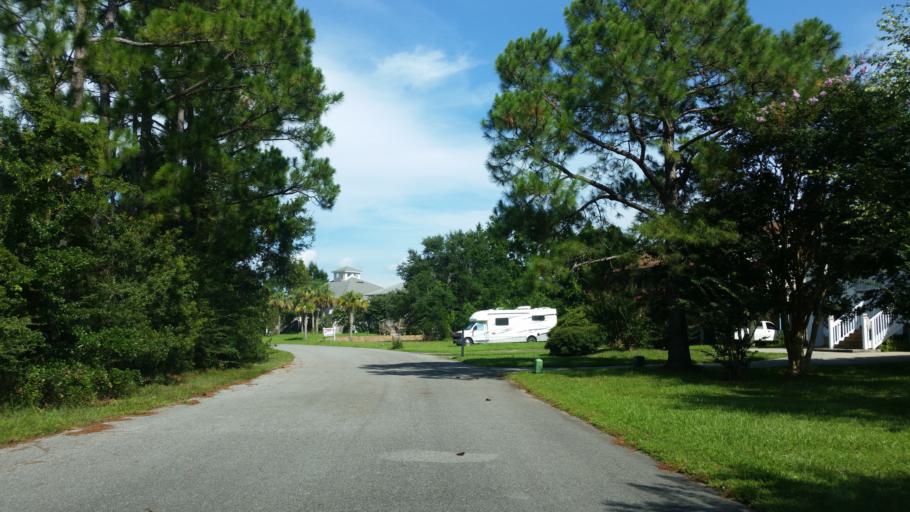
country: US
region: Florida
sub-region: Santa Rosa County
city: Pace
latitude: 30.5811
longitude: -87.1737
